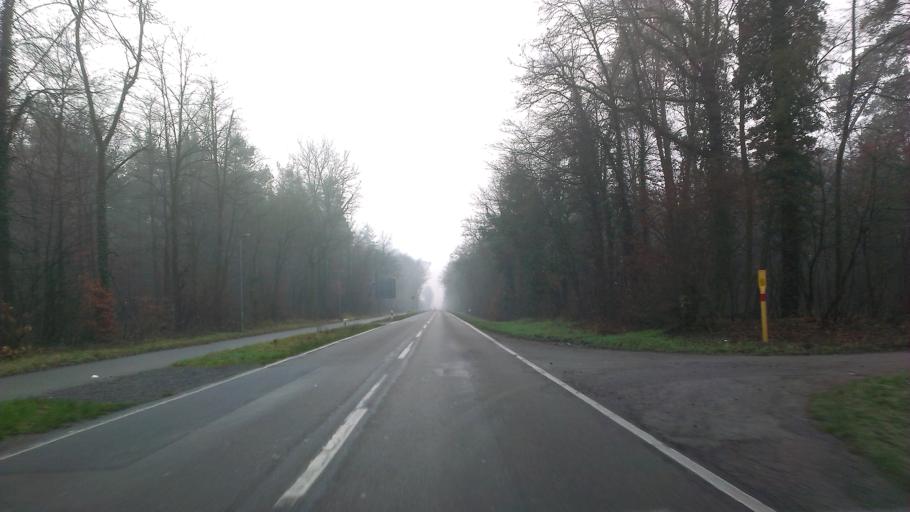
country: DE
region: Baden-Wuerttemberg
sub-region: Karlsruhe Region
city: Waghausel
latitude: 49.2321
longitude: 8.5329
